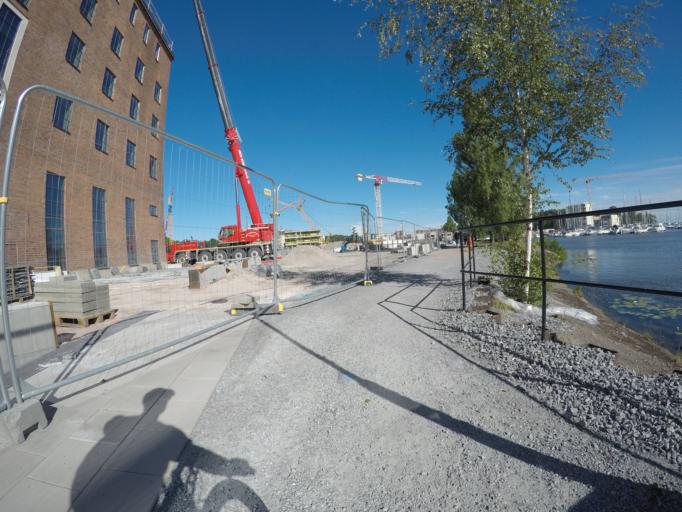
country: SE
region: Vaestmanland
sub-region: Vasteras
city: Vasteras
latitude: 59.6068
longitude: 16.5673
